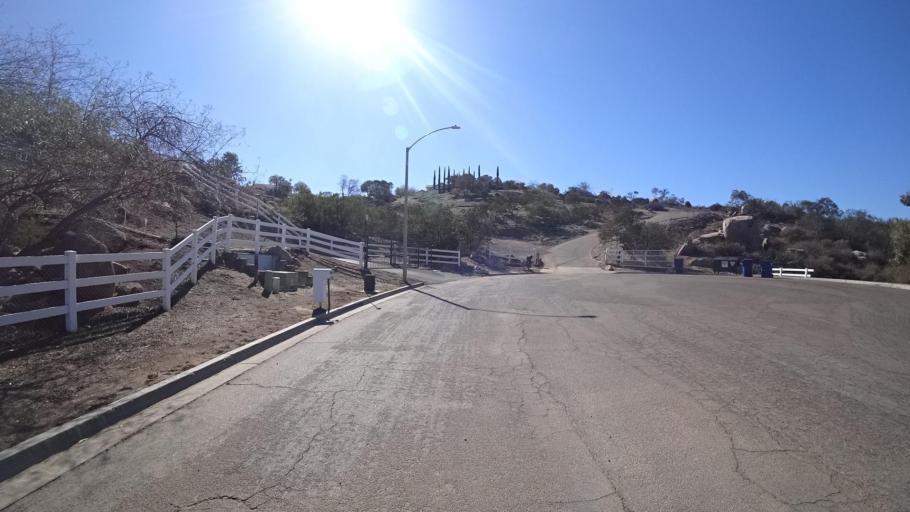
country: US
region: California
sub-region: San Diego County
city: Crest
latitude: 32.8615
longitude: -116.8680
